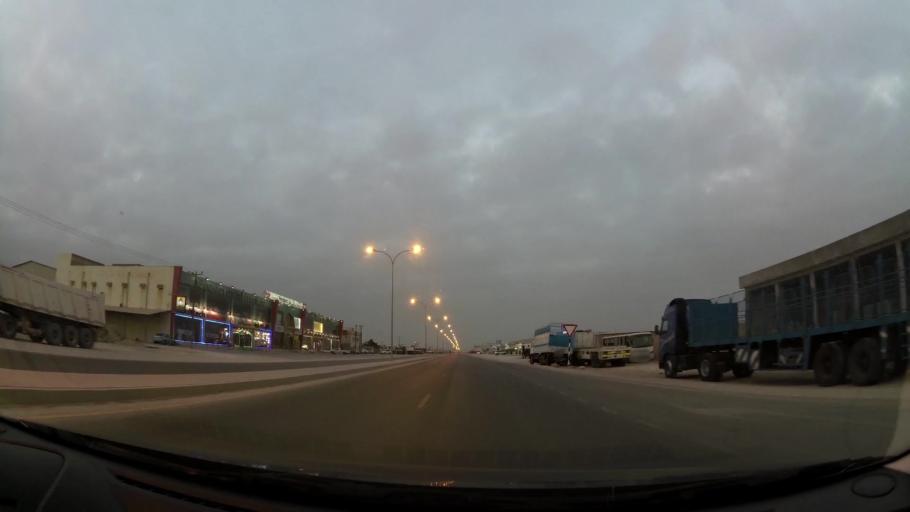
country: OM
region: Zufar
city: Salalah
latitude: 17.0234
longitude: 54.0398
